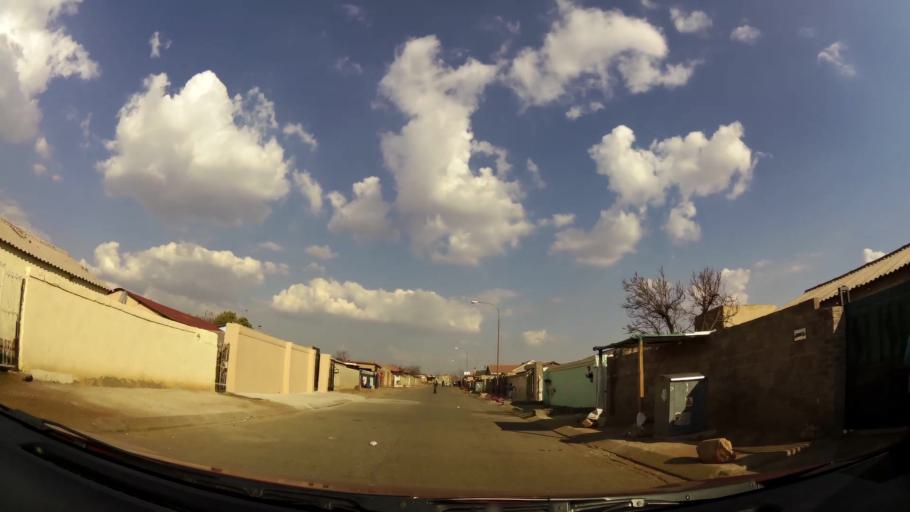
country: ZA
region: Gauteng
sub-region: City of Johannesburg Metropolitan Municipality
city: Soweto
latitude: -26.2277
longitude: 27.8684
